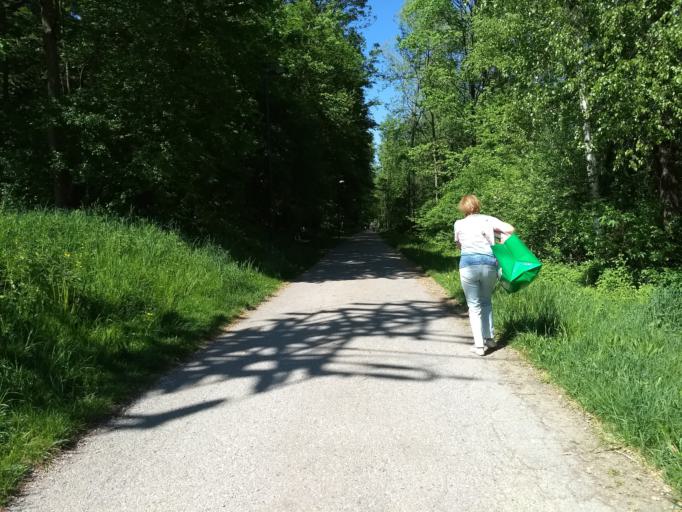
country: AT
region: Salzburg
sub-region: Politischer Bezirk Salzburg-Umgebung
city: Anif
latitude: 47.7765
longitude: 13.0749
